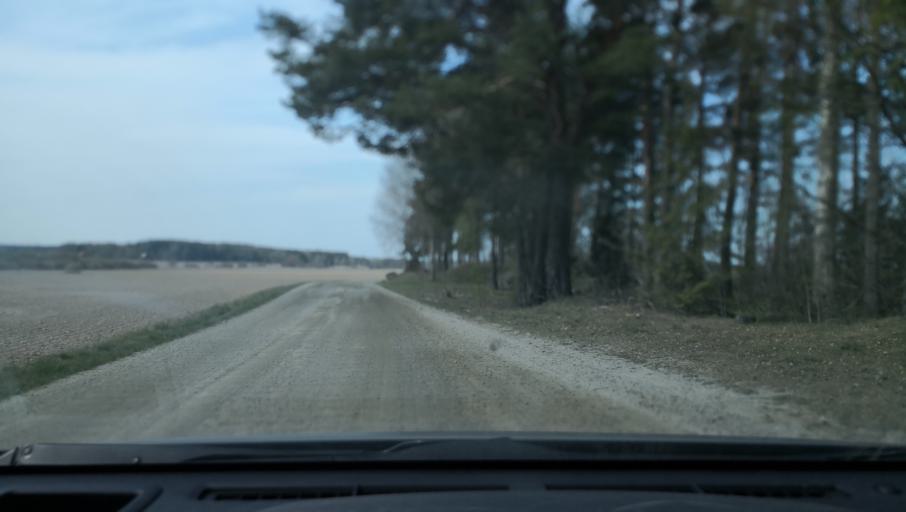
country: SE
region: Vaestmanland
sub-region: Vasteras
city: Skultuna
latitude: 59.7873
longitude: 16.4550
